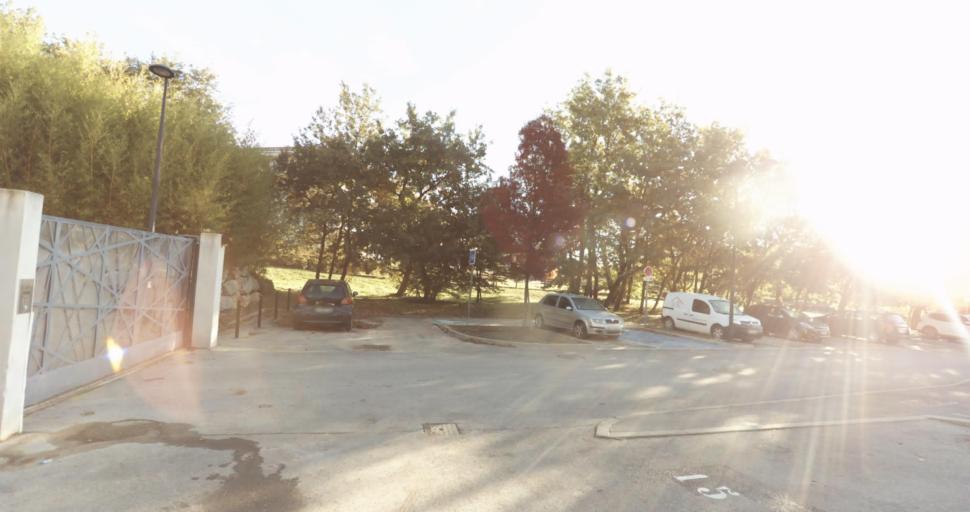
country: FR
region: Provence-Alpes-Cote d'Azur
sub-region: Departement des Bouches-du-Rhone
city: Venelles
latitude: 43.6030
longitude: 5.4767
